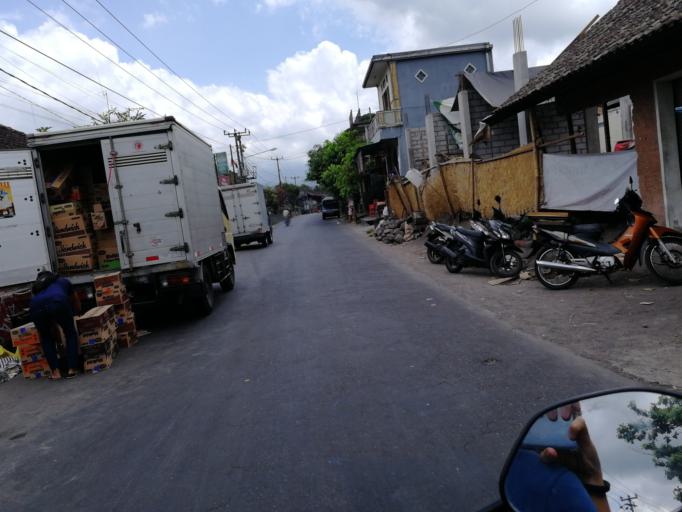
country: ID
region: Bali
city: Banjar Wangsian
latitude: -8.4645
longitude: 115.4478
